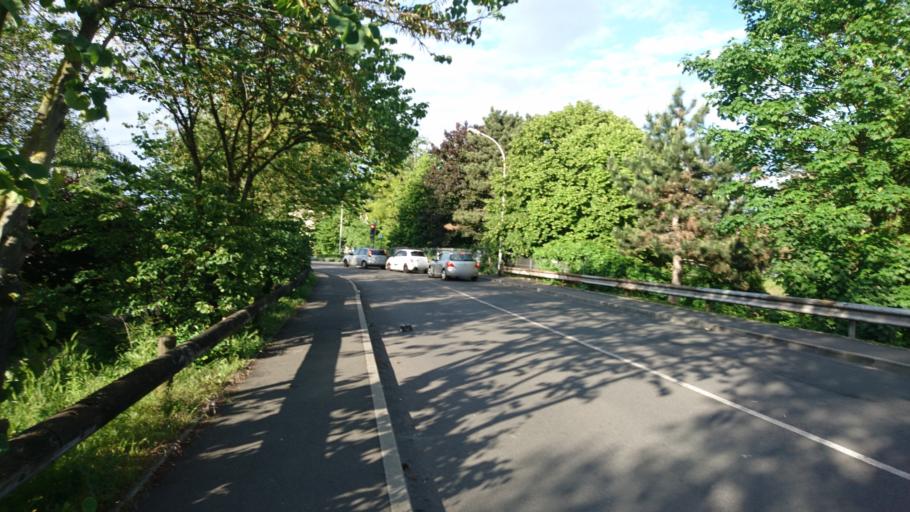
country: FR
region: Ile-de-France
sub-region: Departement du Val-d'Oise
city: Garges-les-Gonesse
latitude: 48.9743
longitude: 2.3875
